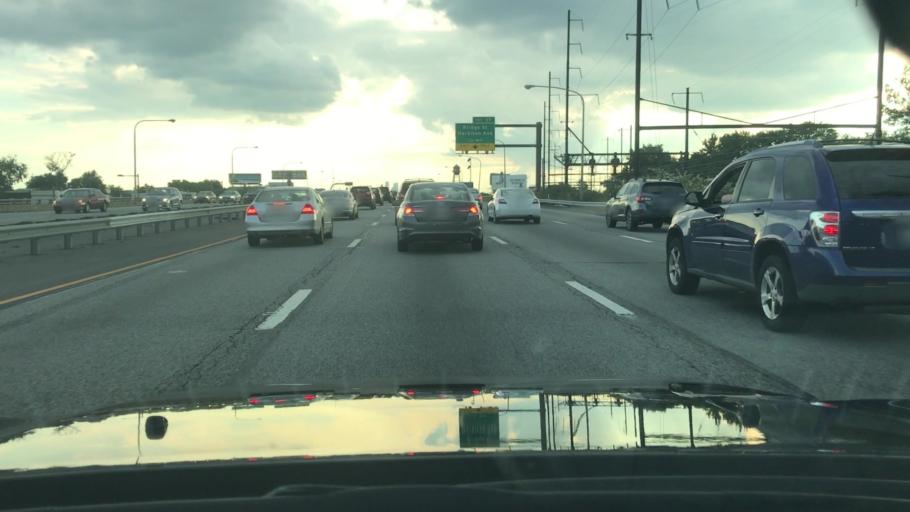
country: US
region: New Jersey
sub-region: Burlington County
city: Palmyra
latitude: 40.0149
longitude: -75.0548
